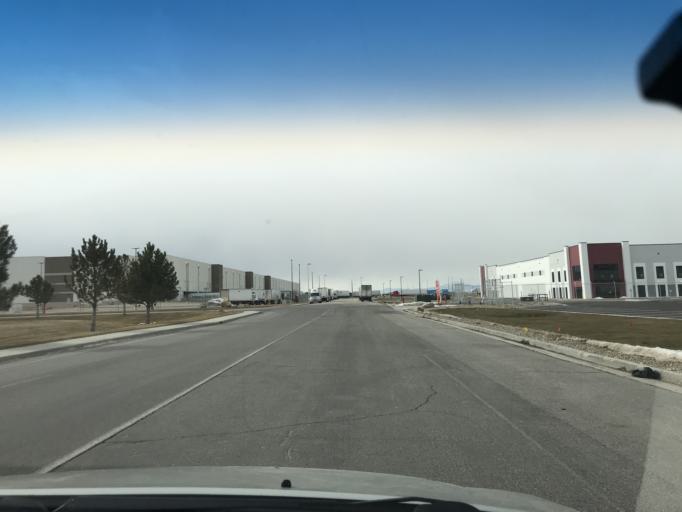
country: US
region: Utah
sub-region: Salt Lake County
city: West Valley City
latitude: 40.7873
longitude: -112.0241
